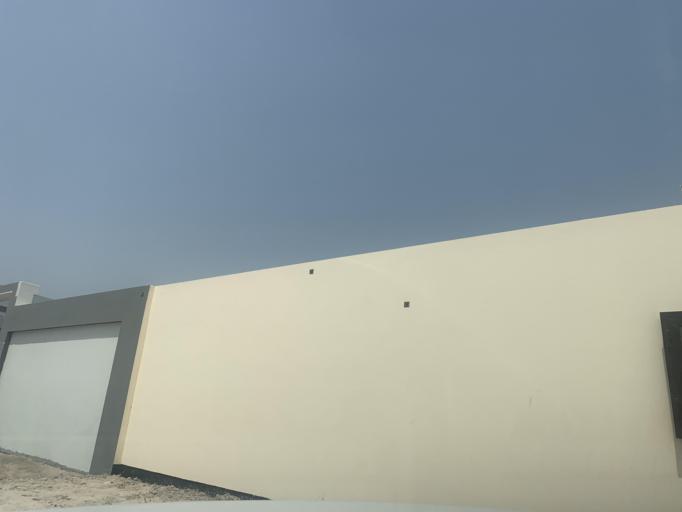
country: BH
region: Central Governorate
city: Madinat Hamad
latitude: 26.1237
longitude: 50.4705
